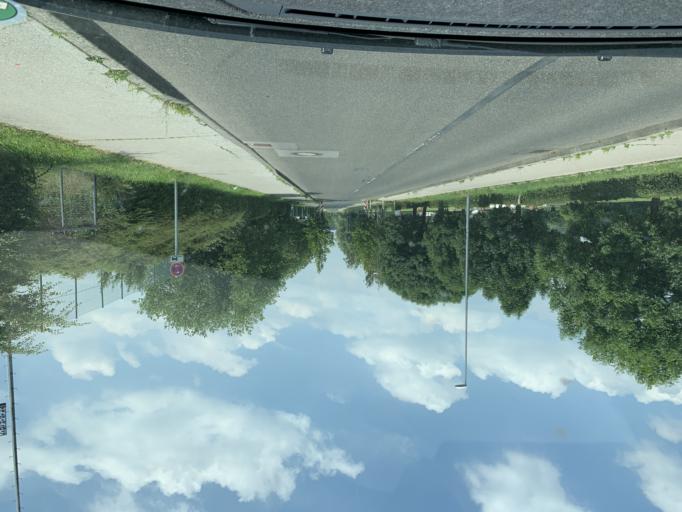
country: DE
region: North Rhine-Westphalia
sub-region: Regierungsbezirk Koln
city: Aachen
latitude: 50.7946
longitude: 6.0914
